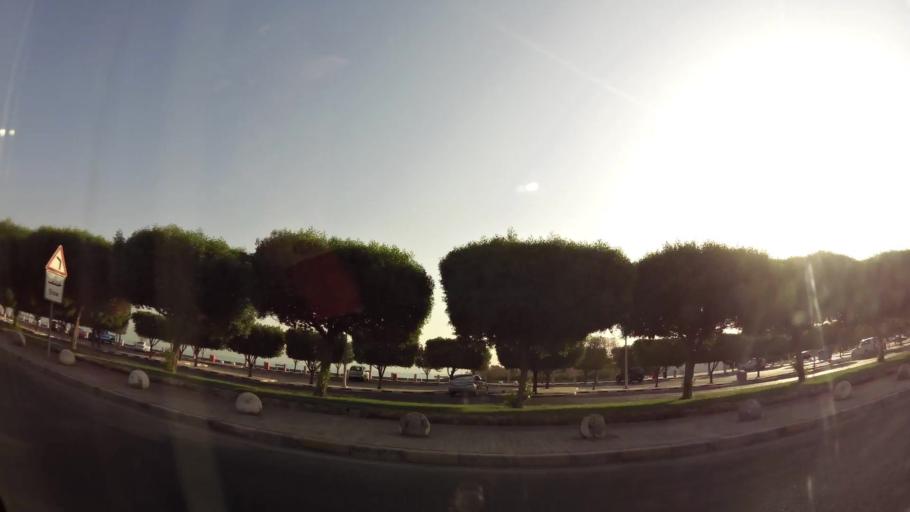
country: KW
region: Al Asimah
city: Ad Dasmah
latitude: 29.3652
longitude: 48.0223
